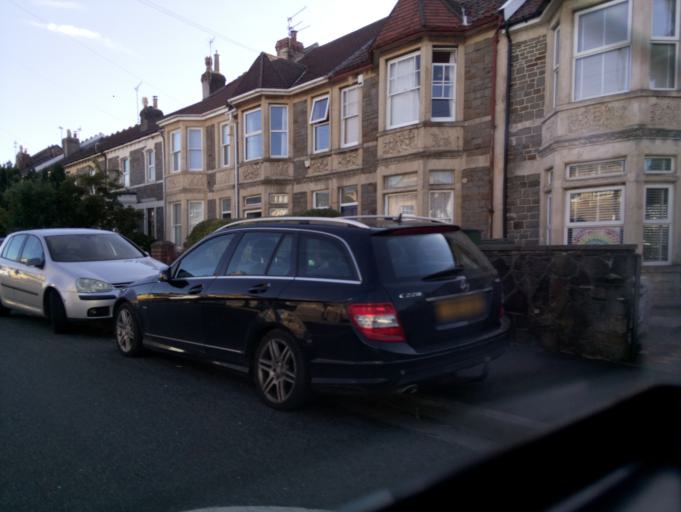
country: GB
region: England
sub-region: Bath and North East Somerset
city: Whitchurch
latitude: 51.4373
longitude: -2.5520
